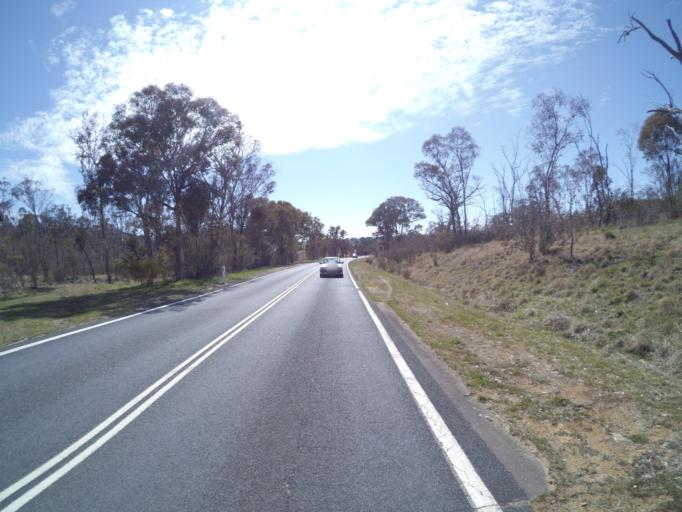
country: AU
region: Australian Capital Territory
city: Macarthur
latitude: -35.4512
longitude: 149.0459
